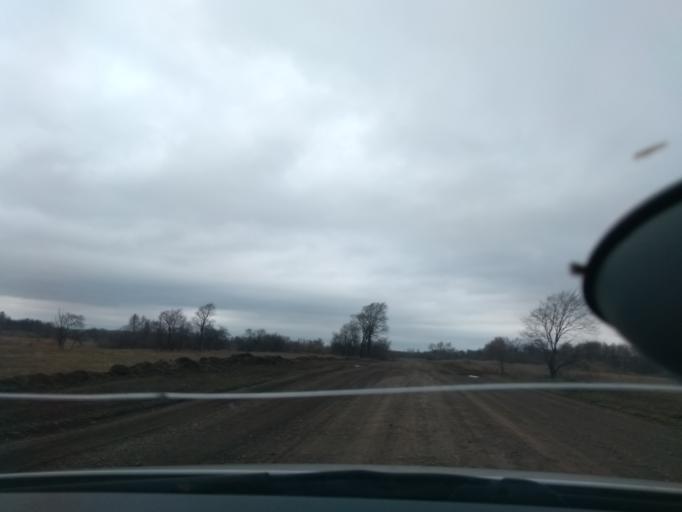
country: RU
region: Perm
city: Orda
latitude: 57.2360
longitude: 56.6109
